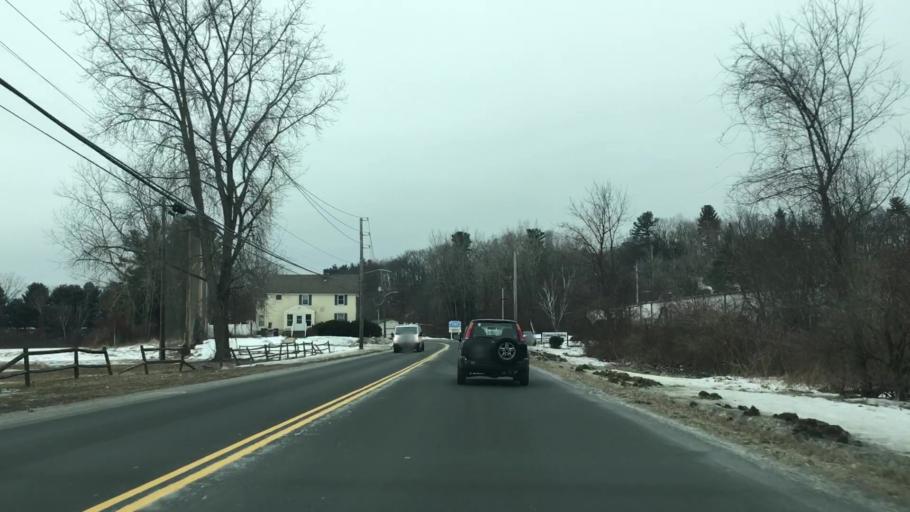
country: US
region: Massachusetts
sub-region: Hampden County
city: Westfield
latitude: 42.1205
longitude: -72.7158
